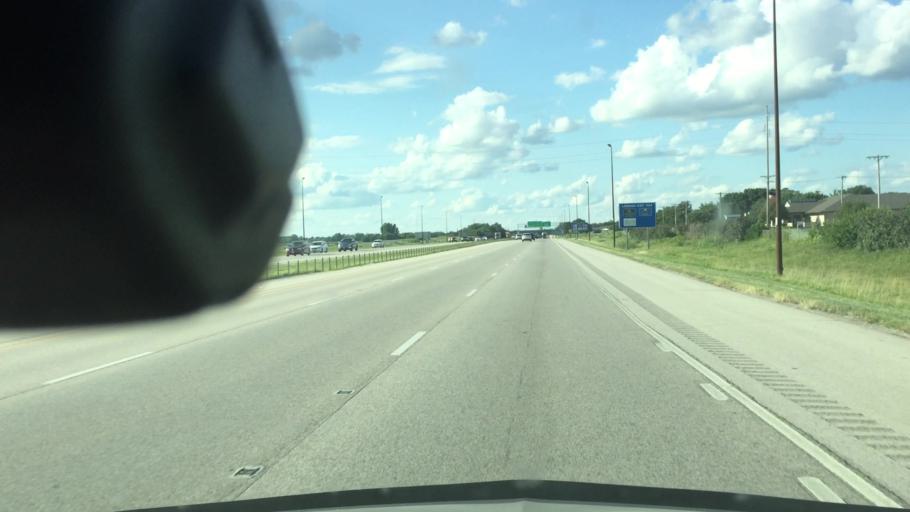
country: US
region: Illinois
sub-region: Sangamon County
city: Southern View
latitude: 39.7191
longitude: -89.6439
